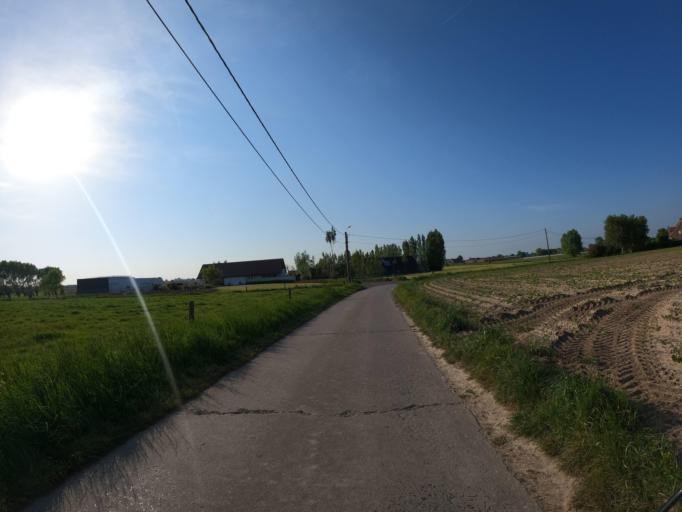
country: BE
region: Flanders
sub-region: Provincie West-Vlaanderen
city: Ruiselede
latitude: 51.0246
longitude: 3.3648
